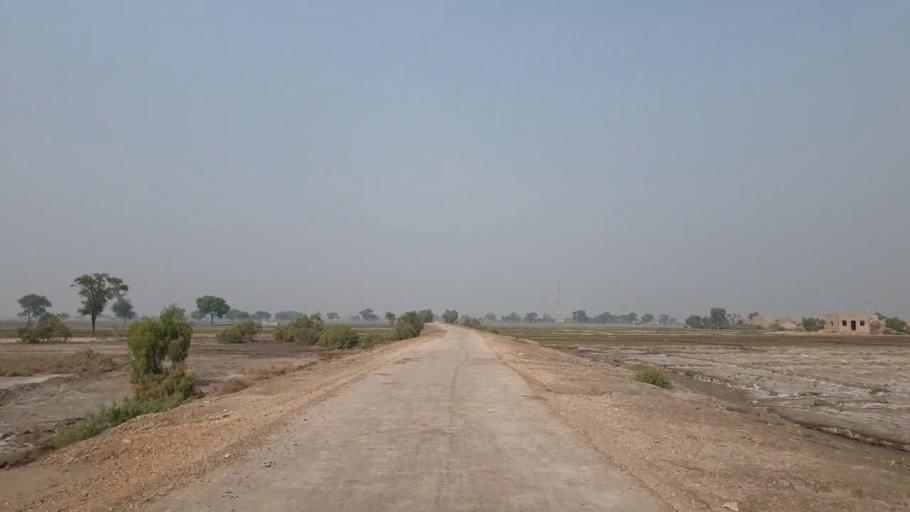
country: PK
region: Sindh
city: Bhan
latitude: 26.4916
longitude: 67.7002
